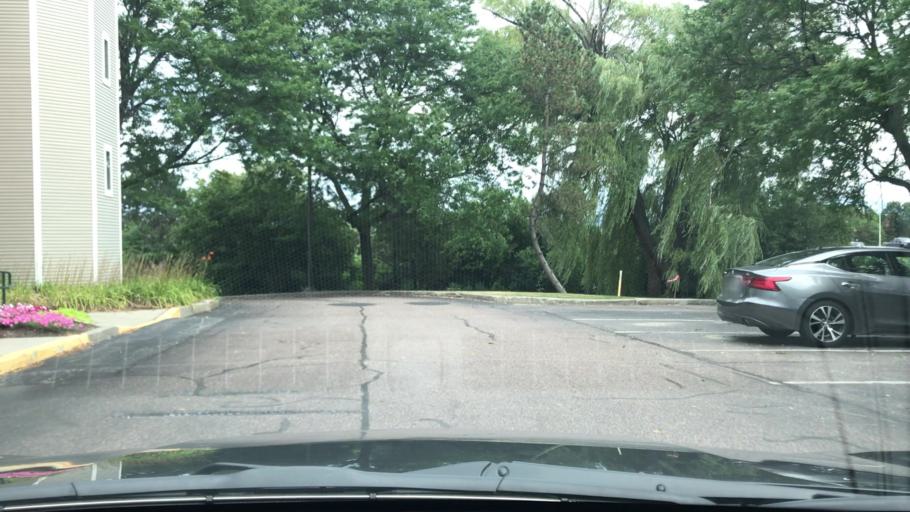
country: US
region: Vermont
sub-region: Chittenden County
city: South Burlington
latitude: 44.4717
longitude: -73.1867
